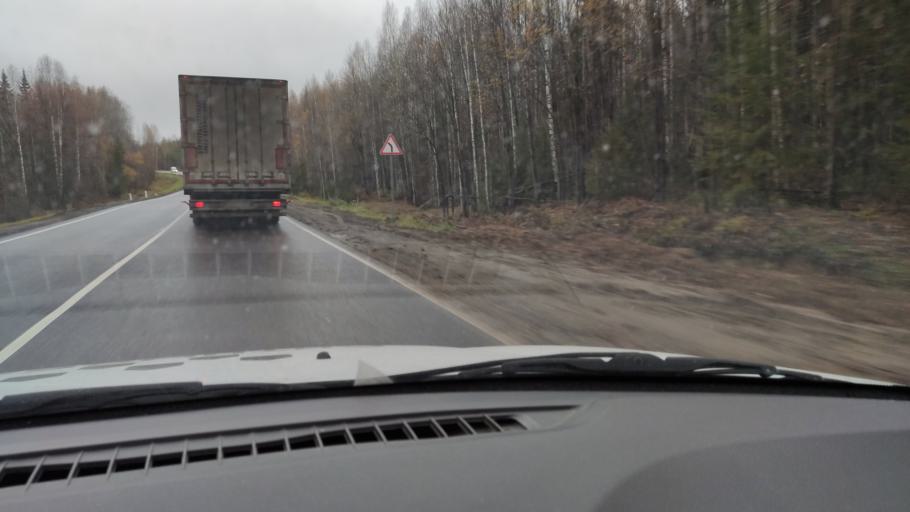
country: RU
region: Kirov
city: Omutninsk
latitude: 58.7464
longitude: 52.0622
